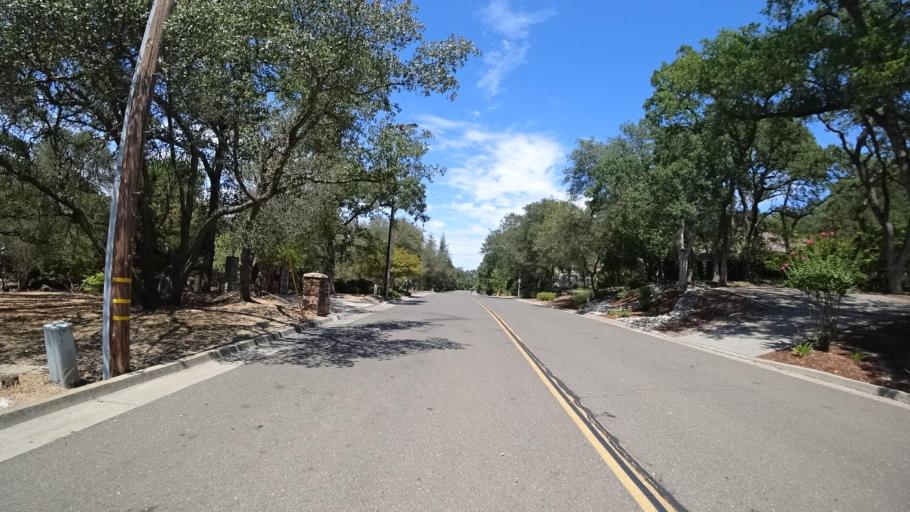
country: US
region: California
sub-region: Placer County
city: Rocklin
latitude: 38.8178
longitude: -121.2319
